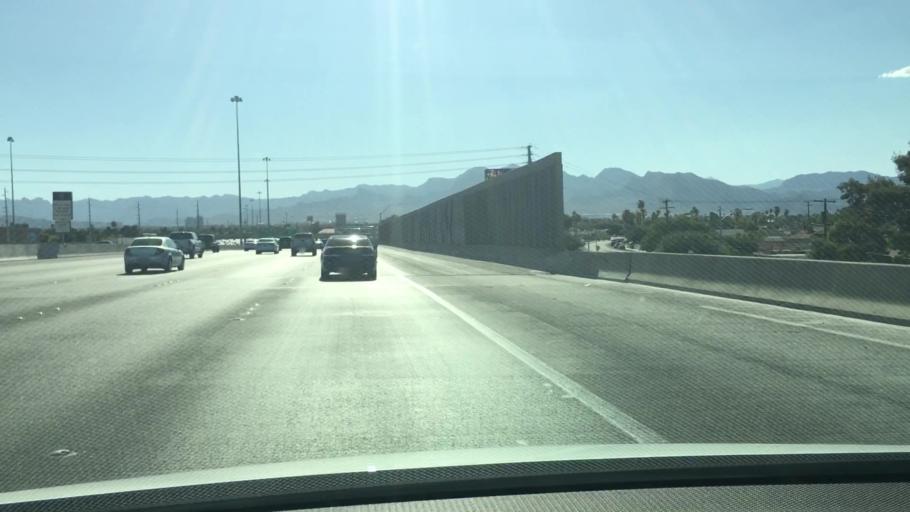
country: US
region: Nevada
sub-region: Clark County
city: Spring Valley
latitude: 36.1748
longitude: -115.2241
